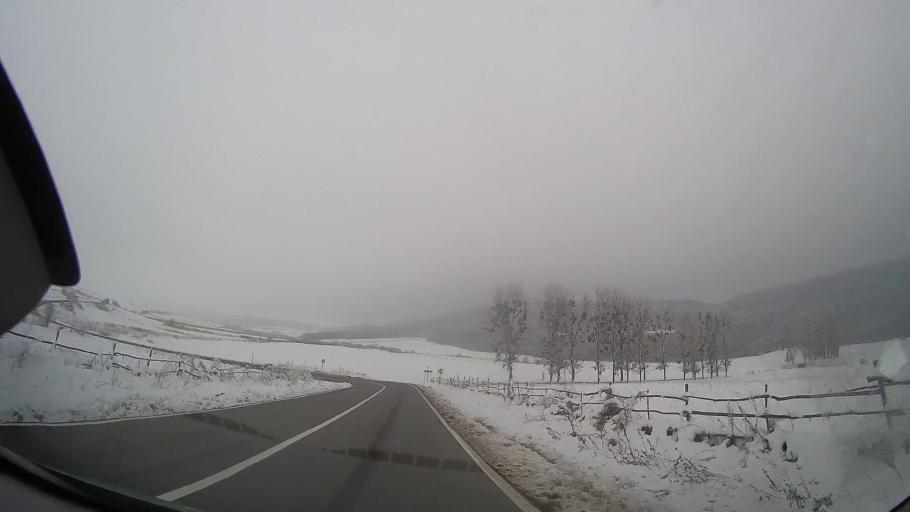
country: RO
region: Neamt
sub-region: Comuna Poenari
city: Poienari
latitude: 46.8738
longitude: 27.1364
